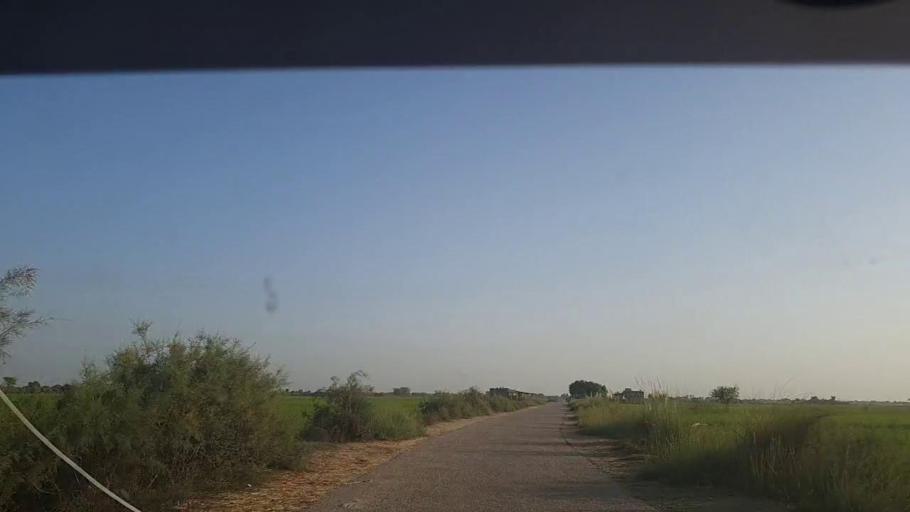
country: PK
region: Sindh
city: Thul
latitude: 28.1978
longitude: 68.8740
